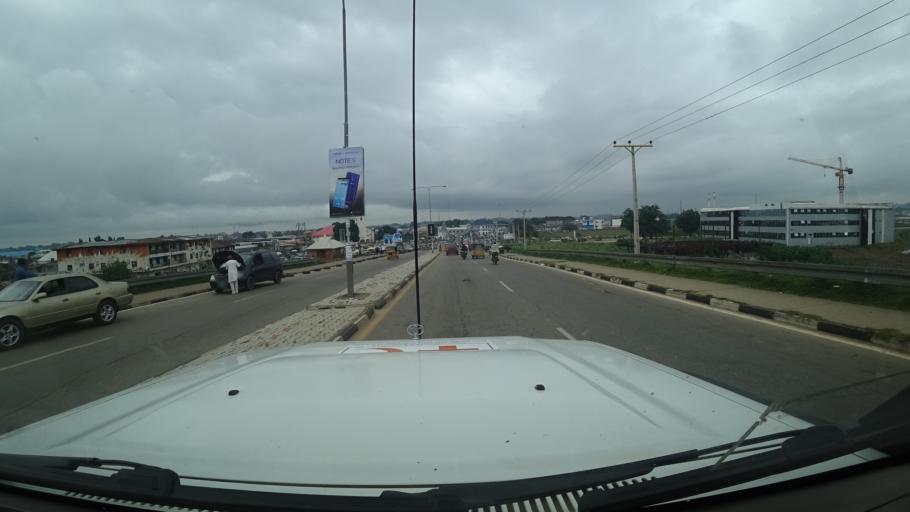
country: NG
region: Niger
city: Minna
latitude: 9.6134
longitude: 6.5486
